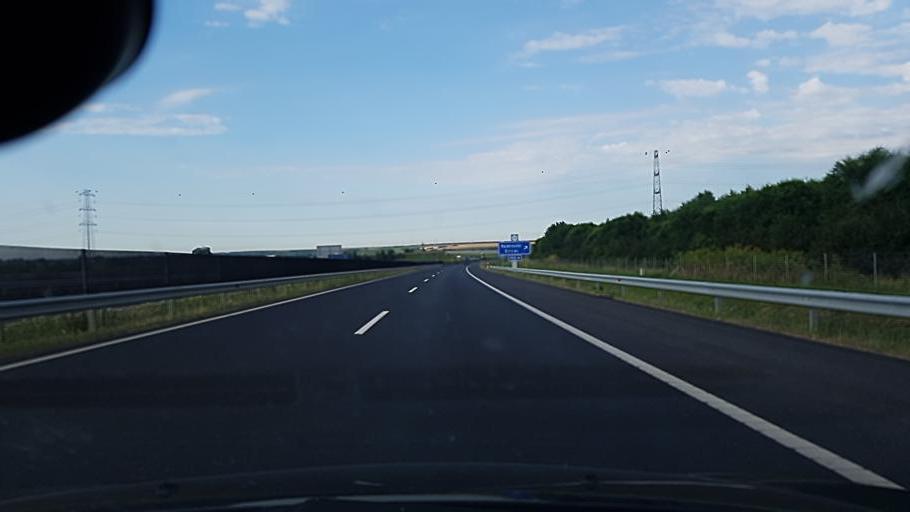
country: HU
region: Fejer
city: Rackeresztur
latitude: 47.2706
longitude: 18.8582
